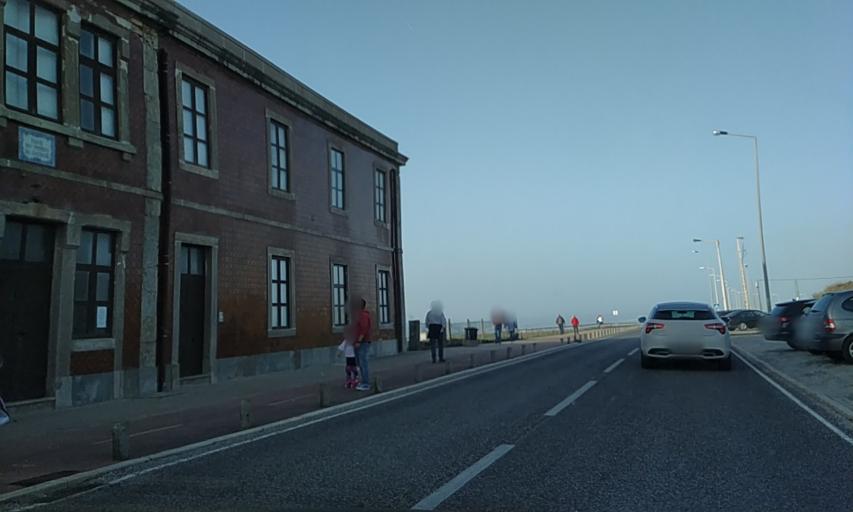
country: PT
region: Leiria
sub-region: Marinha Grande
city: Marinha Grande
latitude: 39.7640
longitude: -9.0308
